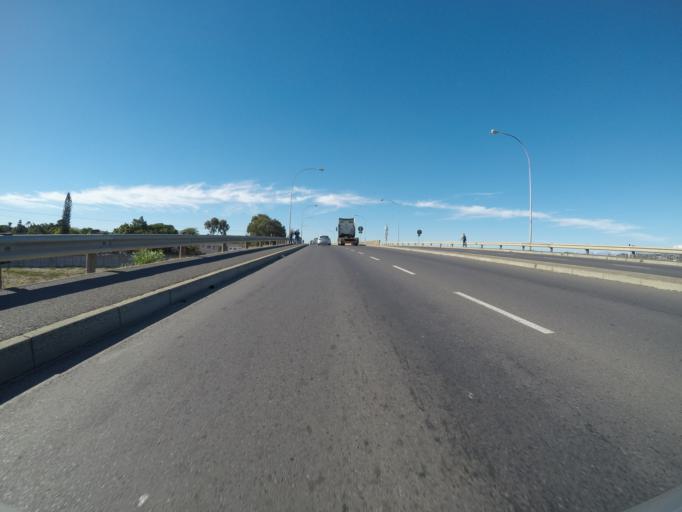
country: ZA
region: Western Cape
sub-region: City of Cape Town
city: Kraaifontein
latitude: -33.8939
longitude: 18.6724
